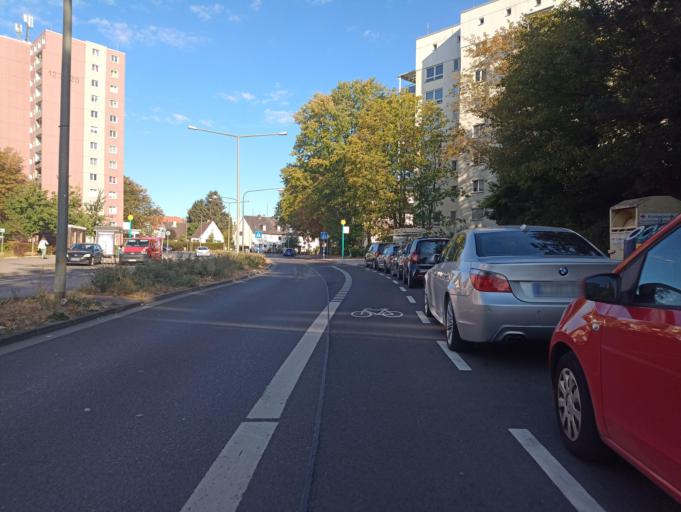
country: DE
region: Hesse
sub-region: Regierungsbezirk Darmstadt
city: Steinbach am Taunus
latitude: 50.1625
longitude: 8.6295
